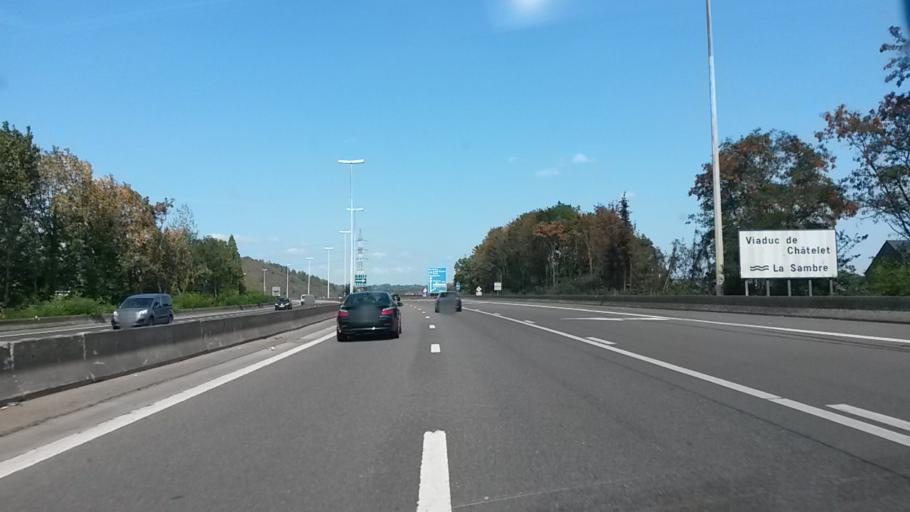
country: BE
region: Wallonia
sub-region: Province du Hainaut
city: Chatelet
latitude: 50.3969
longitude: 4.5089
